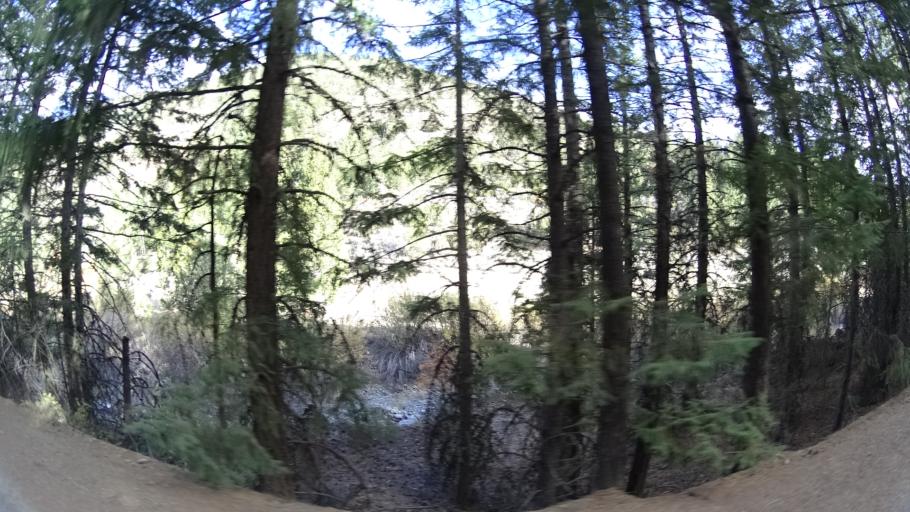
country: US
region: California
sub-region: Siskiyou County
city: Yreka
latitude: 41.7150
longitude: -122.7895
